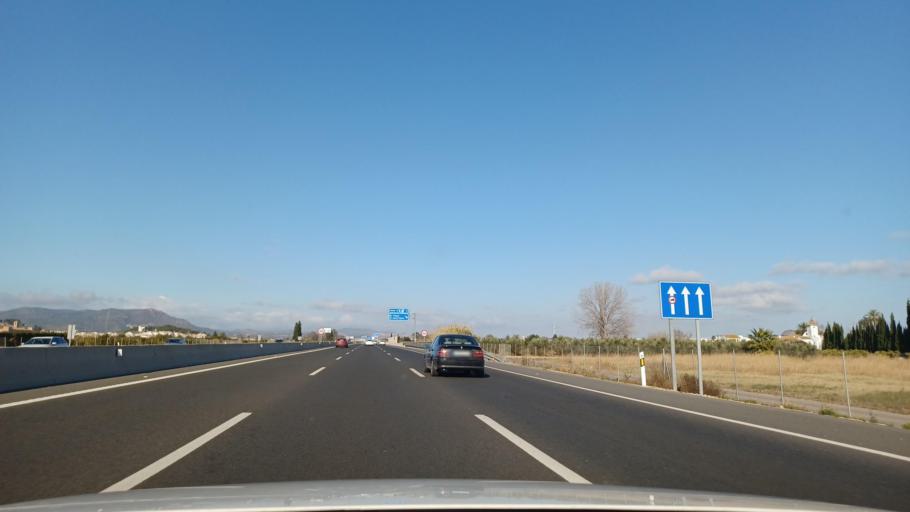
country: ES
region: Valencia
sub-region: Provincia de Valencia
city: Puig
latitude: 39.5723
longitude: -0.2954
